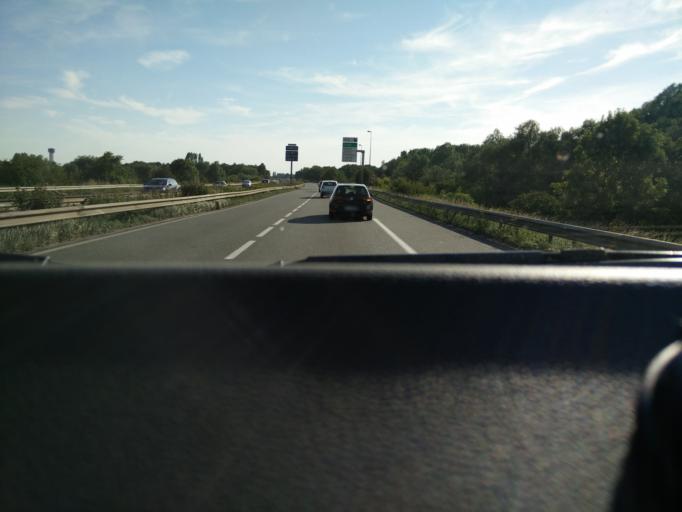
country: FR
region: Nord-Pas-de-Calais
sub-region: Departement du Nord
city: Douchy-les-Mines
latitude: 50.3059
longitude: 3.3791
